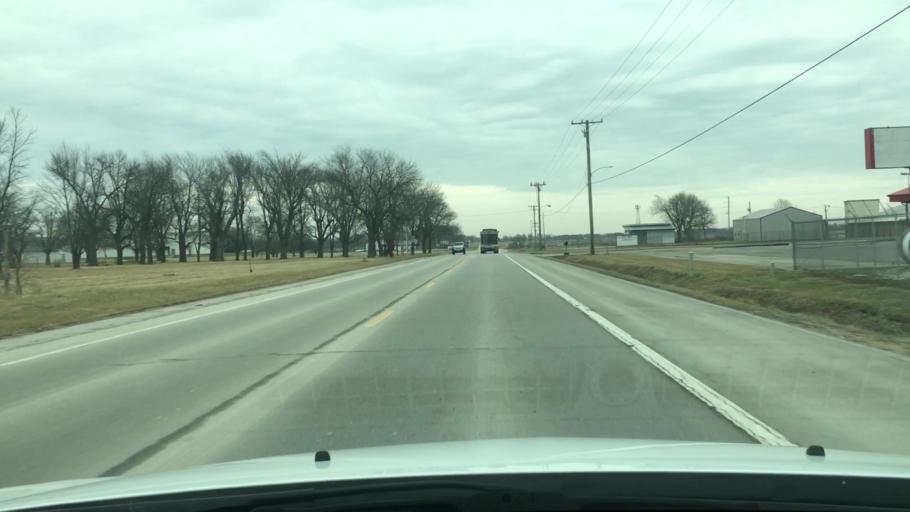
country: US
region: Missouri
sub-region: Audrain County
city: Mexico
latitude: 39.1635
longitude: -91.8262
